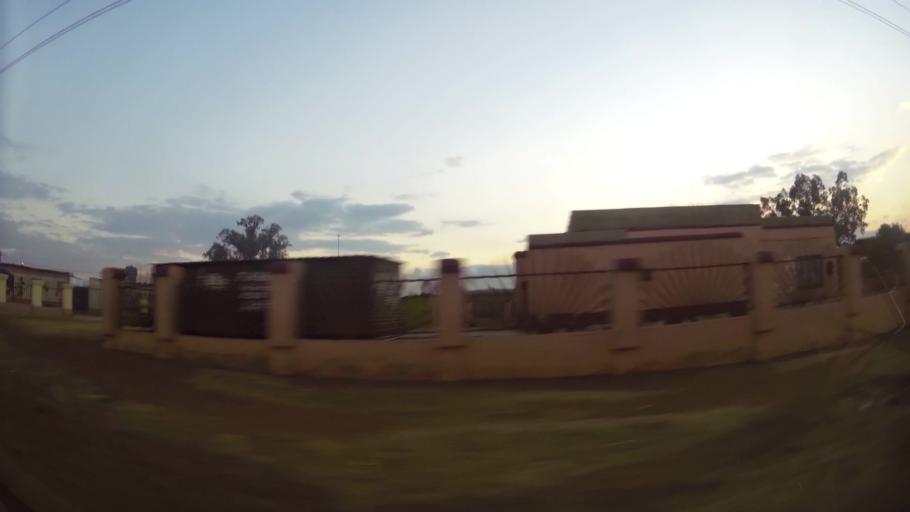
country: ZA
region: Gauteng
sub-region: City of Johannesburg Metropolitan Municipality
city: Orange Farm
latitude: -26.5520
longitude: 27.8599
